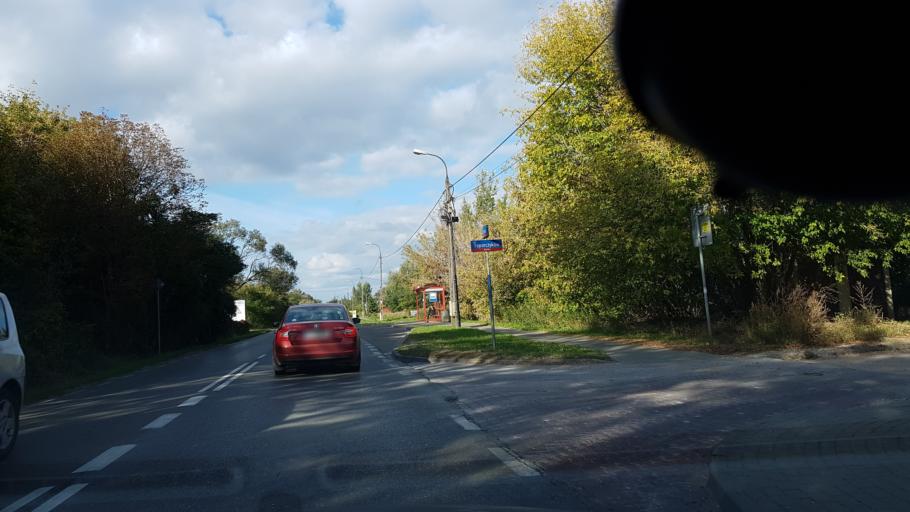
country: PL
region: Masovian Voivodeship
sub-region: Warszawa
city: Targowek
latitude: 52.3035
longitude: 21.0299
